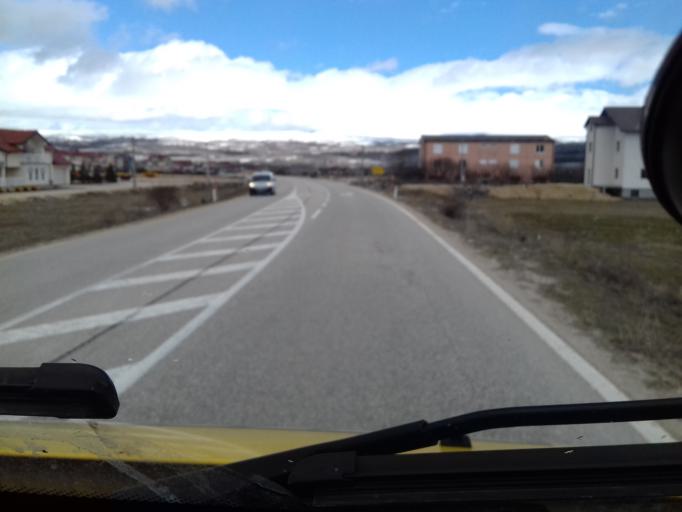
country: BA
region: Federation of Bosnia and Herzegovina
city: Tomislavgrad
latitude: 43.7085
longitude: 17.2360
